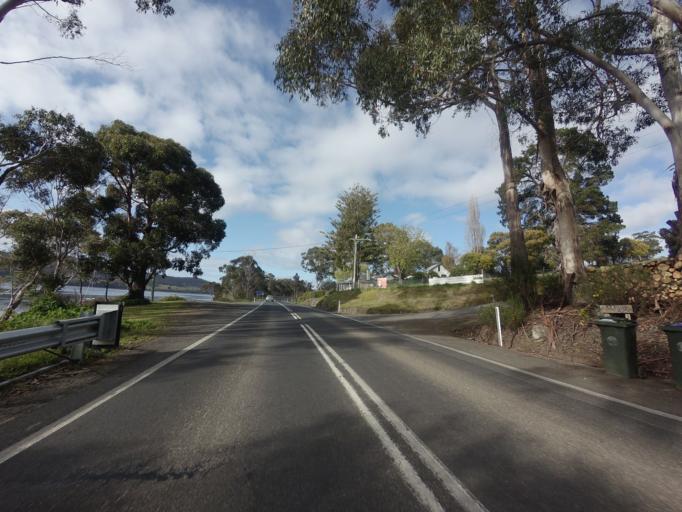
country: AU
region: Tasmania
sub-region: Huon Valley
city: Geeveston
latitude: -43.1543
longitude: 146.9803
